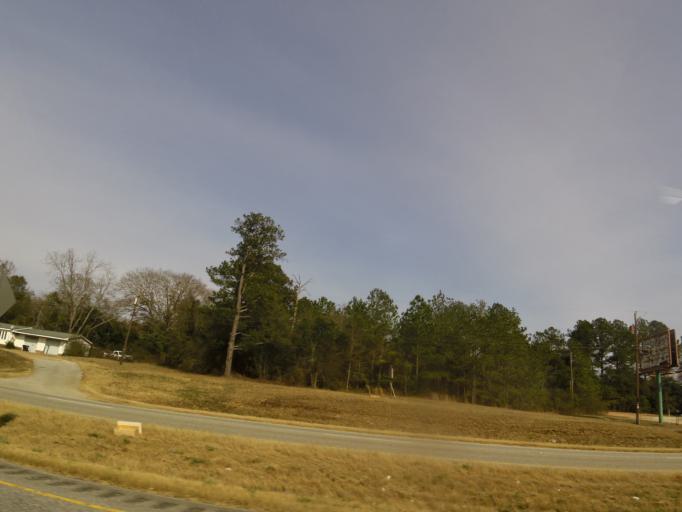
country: US
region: Alabama
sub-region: Dale County
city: Midland City
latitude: 31.2957
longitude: -85.4795
